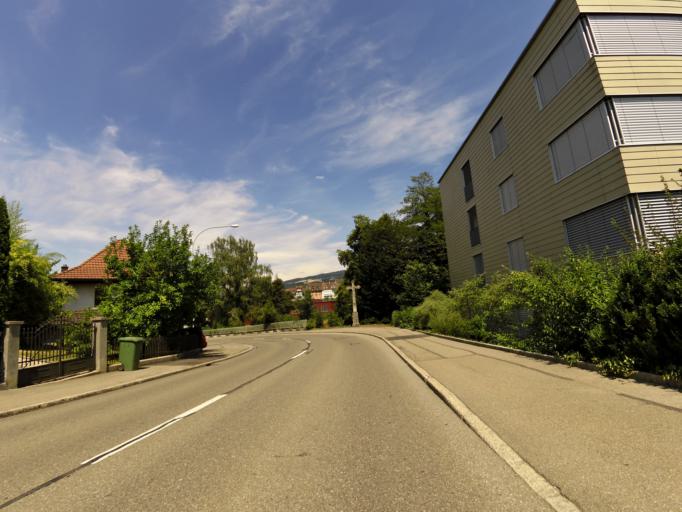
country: CH
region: Aargau
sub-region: Bezirk Bremgarten
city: Bremgarten
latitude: 47.3475
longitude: 8.3404
